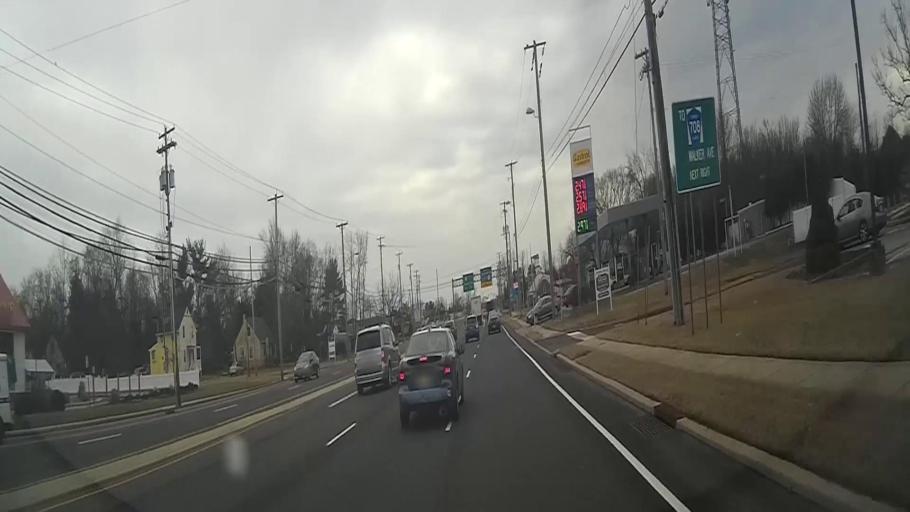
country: US
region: New Jersey
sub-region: Camden County
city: Berlin
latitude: 39.8051
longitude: -74.9317
